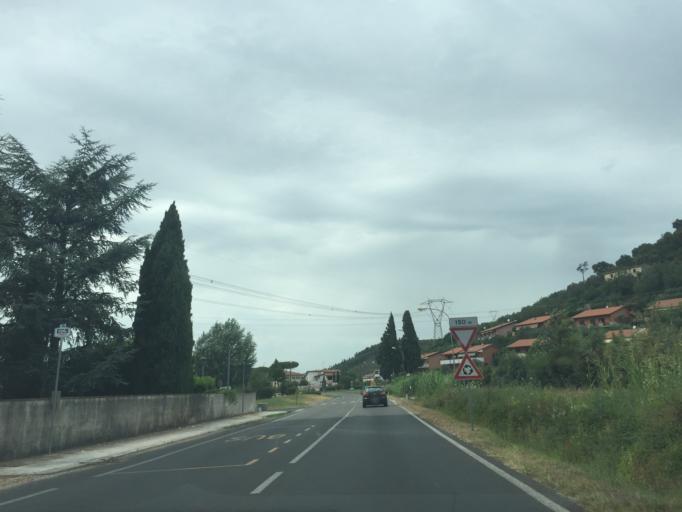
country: IT
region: Tuscany
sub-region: Province of Pisa
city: Gabella
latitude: 43.7218
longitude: 10.5023
